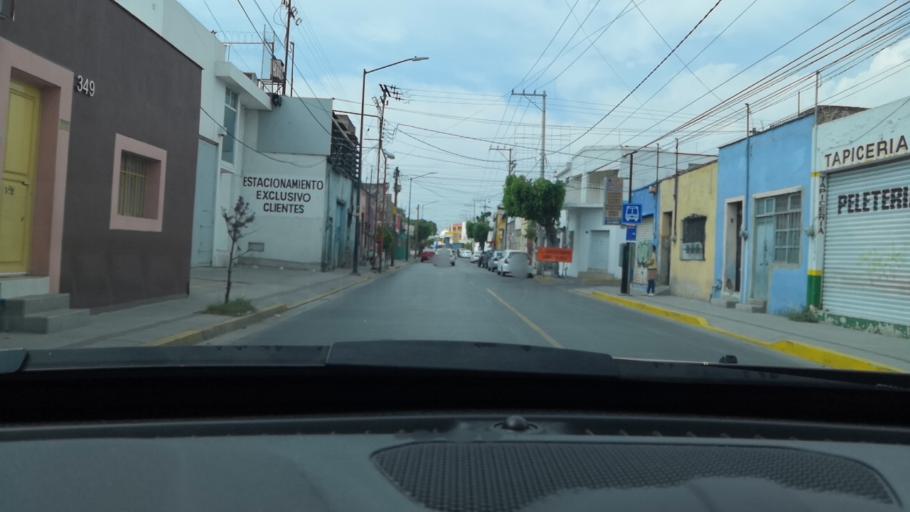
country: MX
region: Guanajuato
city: Leon
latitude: 21.1148
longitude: -101.6767
